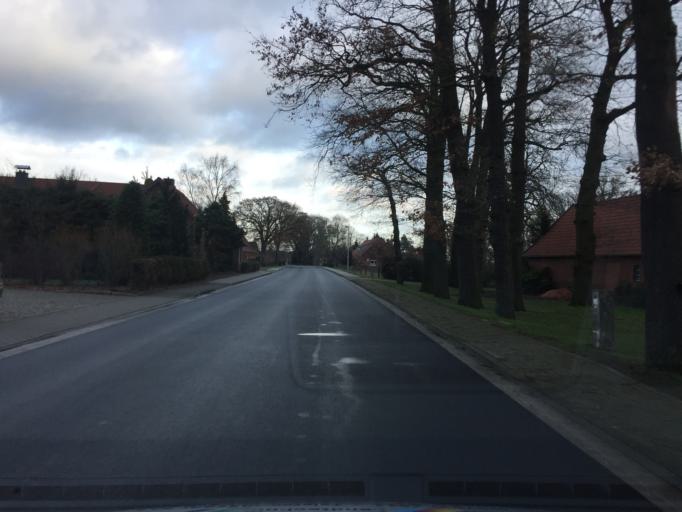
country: DE
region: Lower Saxony
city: Raddestorf
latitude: 52.5057
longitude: 8.9932
